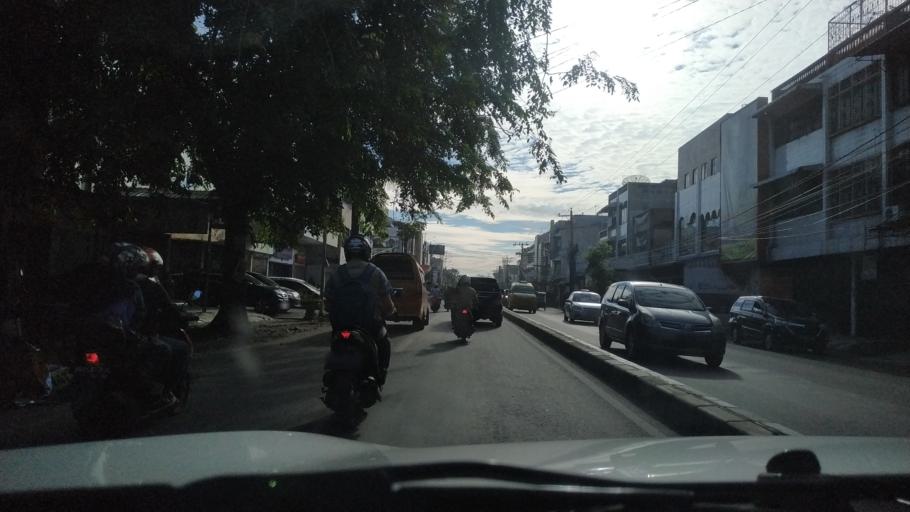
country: ID
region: North Sumatra
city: Medan
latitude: 3.5981
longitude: 98.7020
